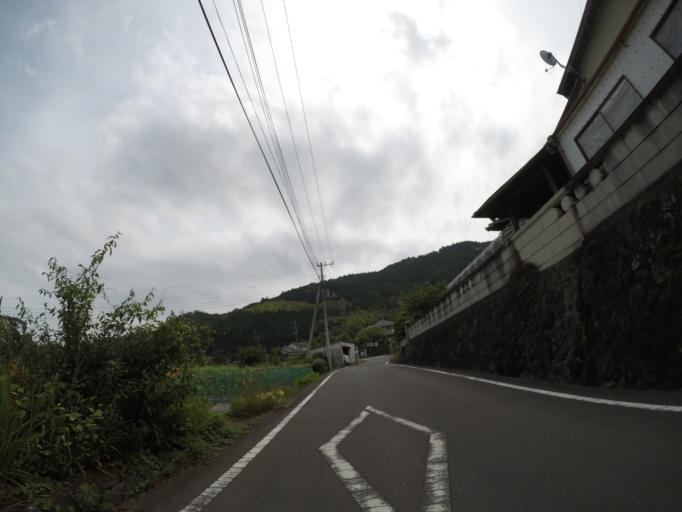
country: JP
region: Shizuoka
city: Fujinomiya
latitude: 35.2566
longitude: 138.5529
